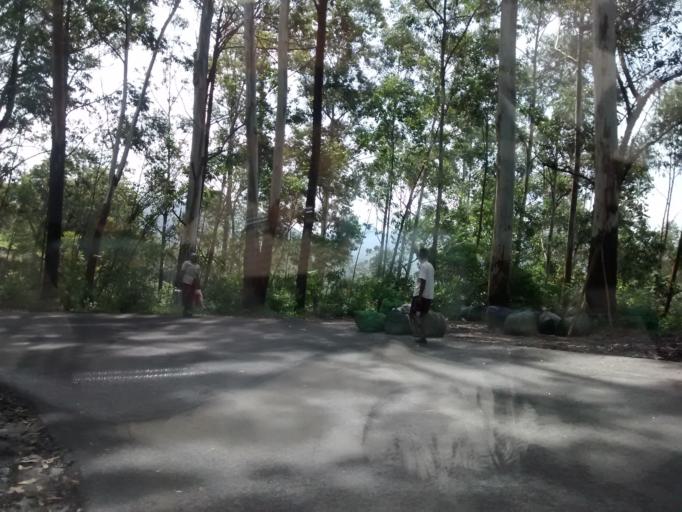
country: IN
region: Kerala
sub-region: Idukki
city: Munnar
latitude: 10.0933
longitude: 77.0922
